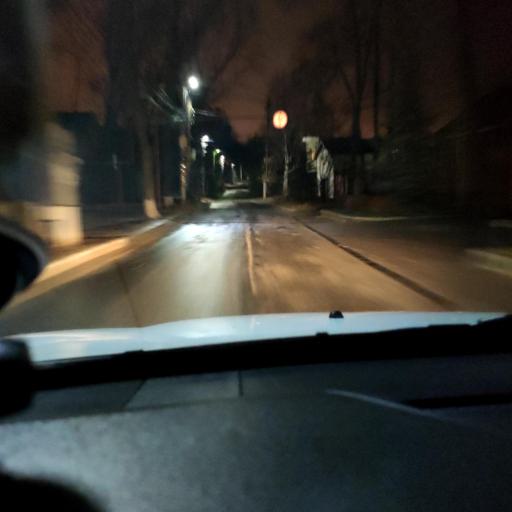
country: RU
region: Samara
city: Samara
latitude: 53.2940
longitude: 50.2003
